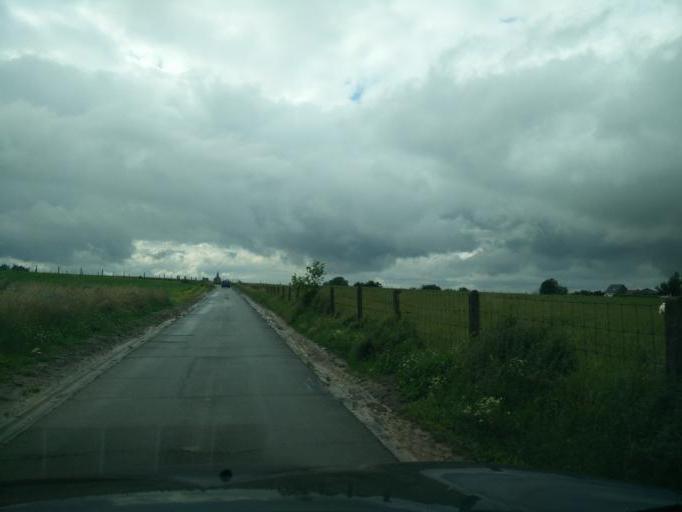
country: BE
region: Flanders
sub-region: Provincie Vlaams-Brabant
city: Pepingen
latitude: 50.7546
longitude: 4.1672
